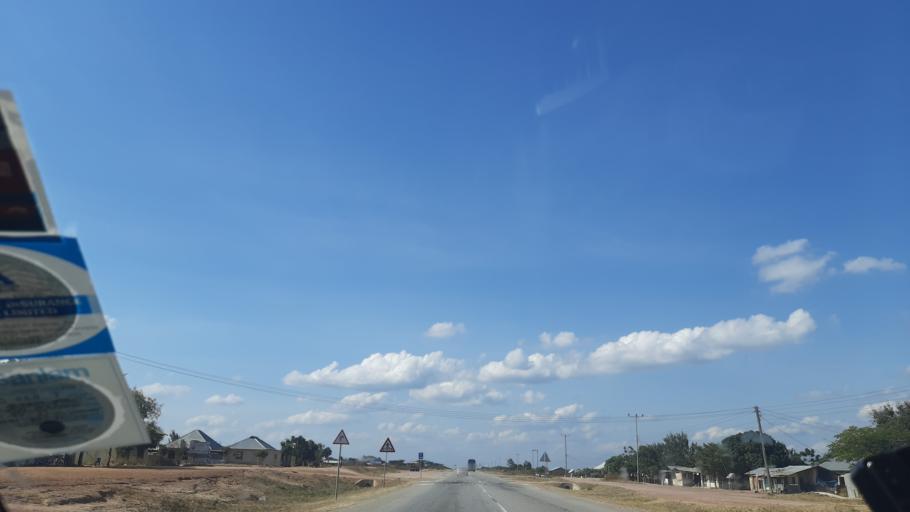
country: TZ
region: Singida
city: Itigi
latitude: -5.5456
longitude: 34.6684
